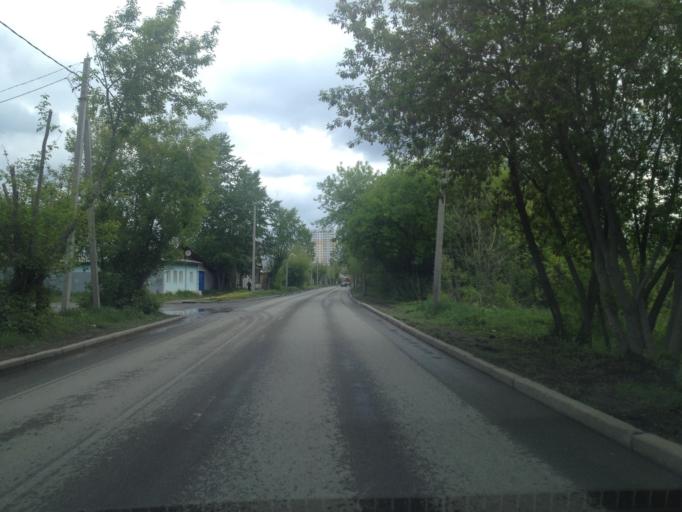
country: RU
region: Sverdlovsk
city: Yekaterinburg
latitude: 56.7774
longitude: 60.6408
